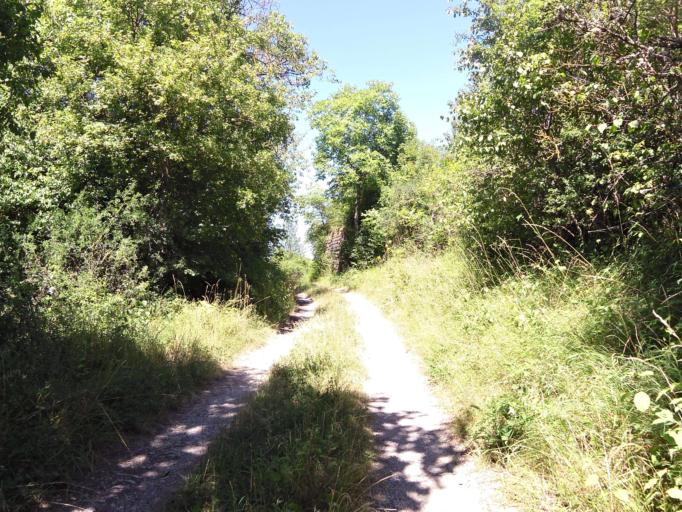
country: DE
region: Bavaria
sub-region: Regierungsbezirk Unterfranken
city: Gerbrunn
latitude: 49.7688
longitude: 9.9995
